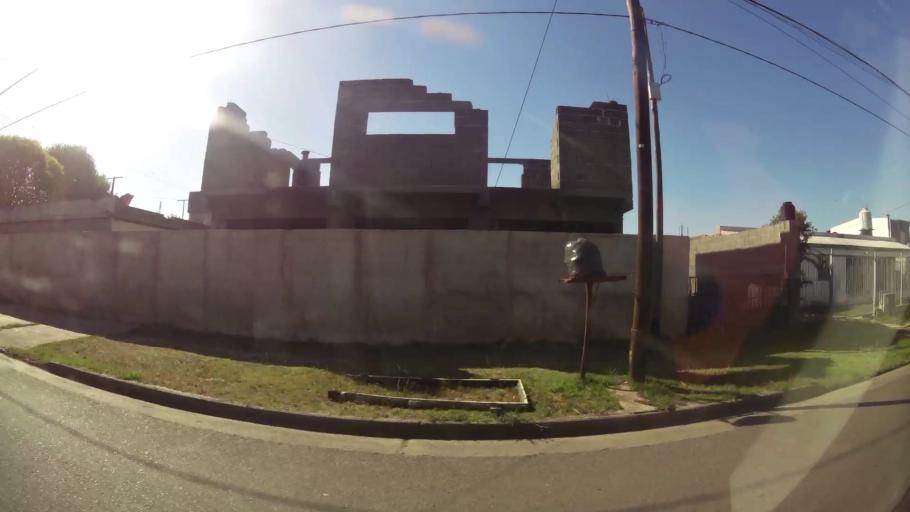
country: AR
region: Cordoba
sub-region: Departamento de Capital
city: Cordoba
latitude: -31.3630
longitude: -64.1884
